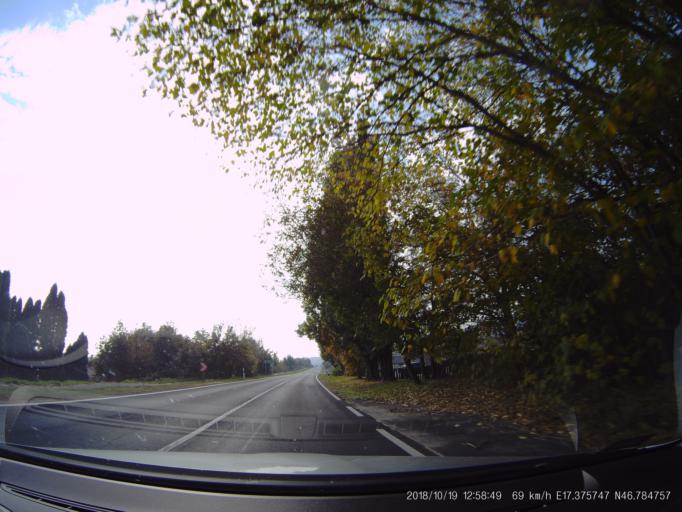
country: HU
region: Zala
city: Vonyarcvashegy
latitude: 46.7847
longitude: 17.3757
